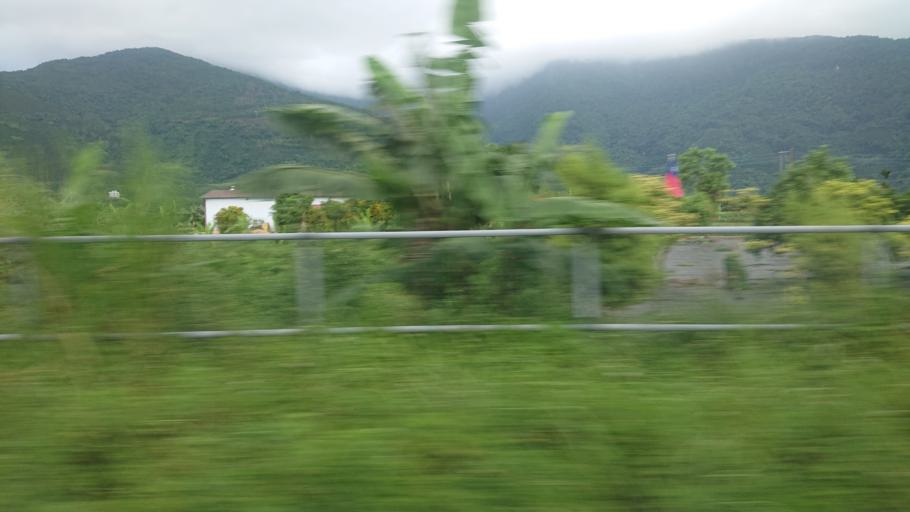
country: TW
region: Taiwan
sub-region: Hualien
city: Hualian
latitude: 23.7411
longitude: 121.4441
